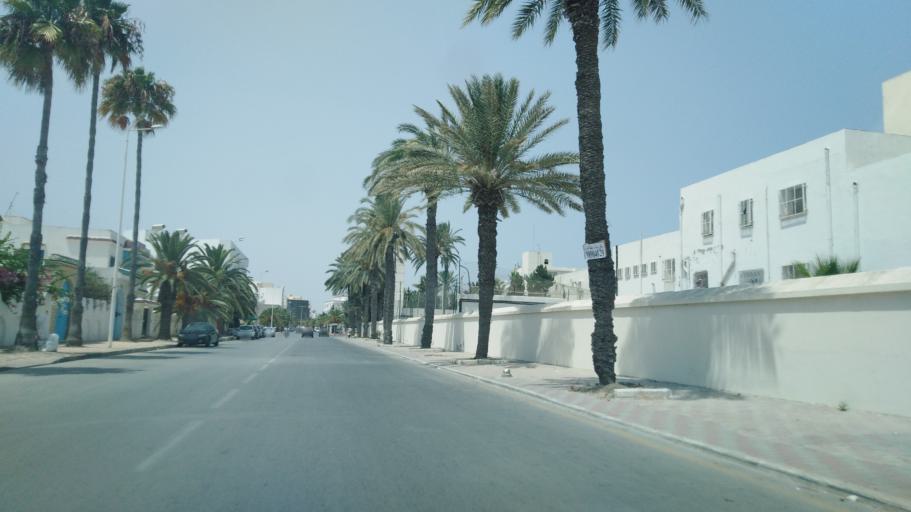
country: TN
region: Al Mahdiyah
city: Mahdia
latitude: 35.5161
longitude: 11.0453
